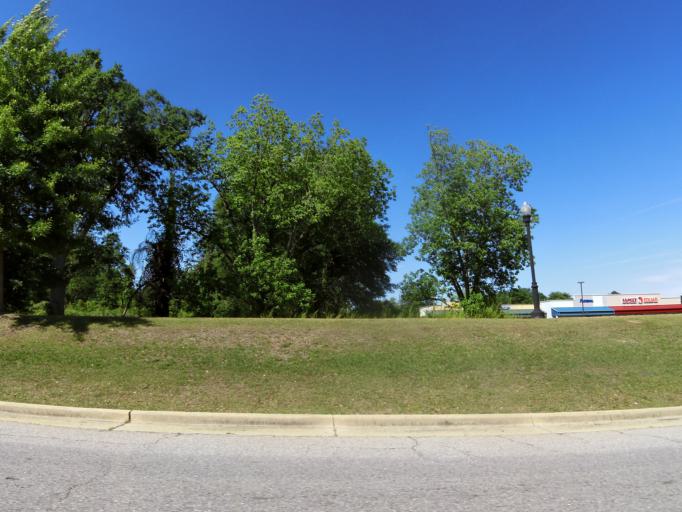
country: US
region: South Carolina
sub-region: Barnwell County
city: Williston
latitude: 33.3989
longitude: -81.4167
